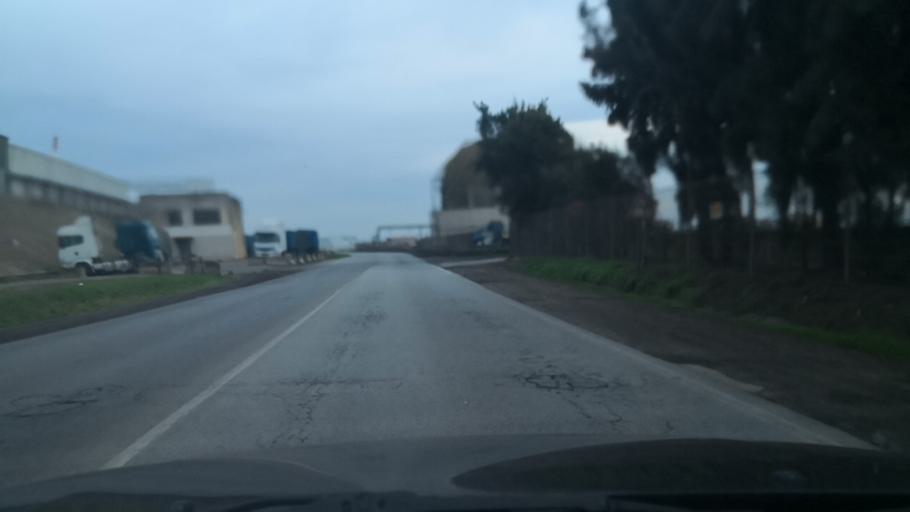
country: PT
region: Setubal
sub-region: Setubal
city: Setubal
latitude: 38.5011
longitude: -8.8411
